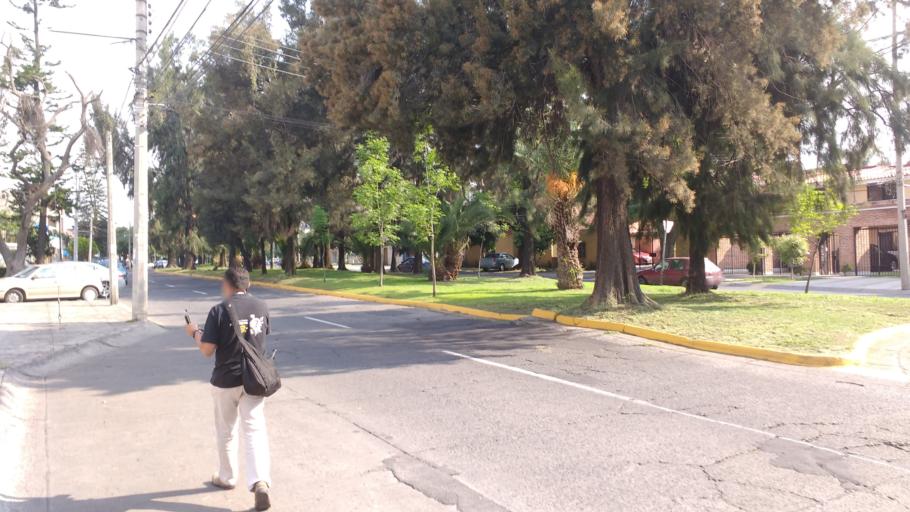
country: MX
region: Jalisco
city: Guadalajara
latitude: 20.6514
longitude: -103.3934
